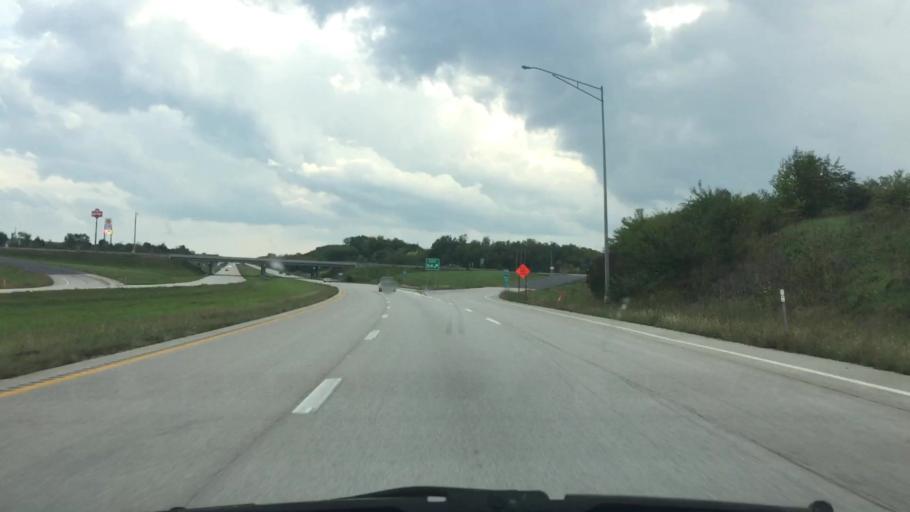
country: US
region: Missouri
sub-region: Clinton County
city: Cameron
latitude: 39.7569
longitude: -94.2197
